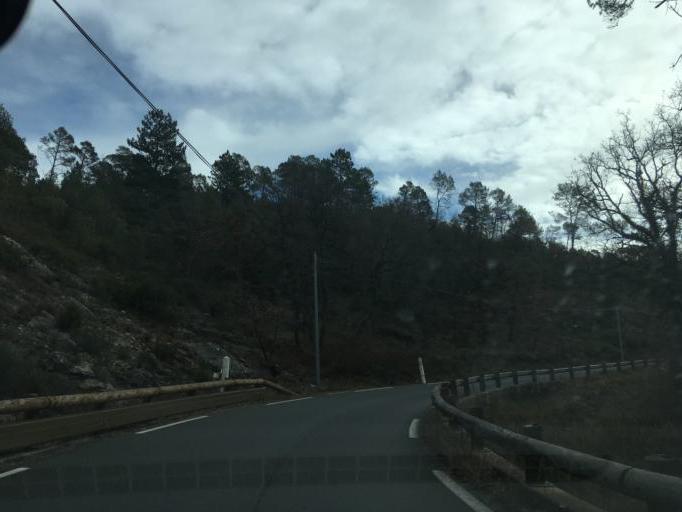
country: FR
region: Provence-Alpes-Cote d'Azur
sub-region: Departement du Var
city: Bras
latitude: 43.4577
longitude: 5.9691
